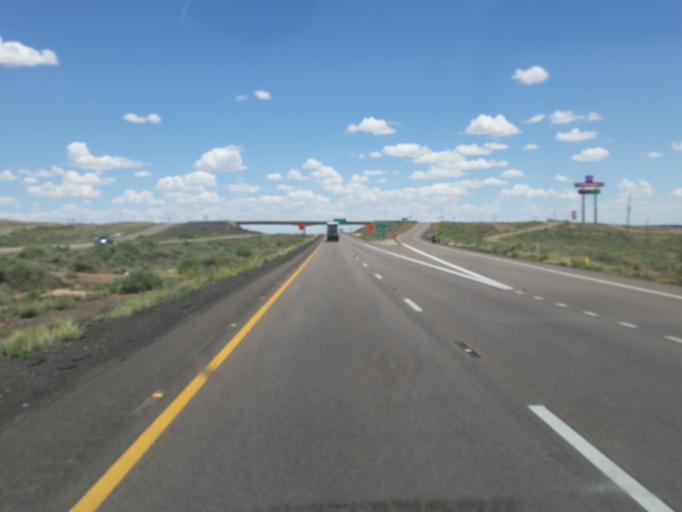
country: US
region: Arizona
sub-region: Navajo County
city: Holbrook
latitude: 34.9078
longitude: -110.2171
